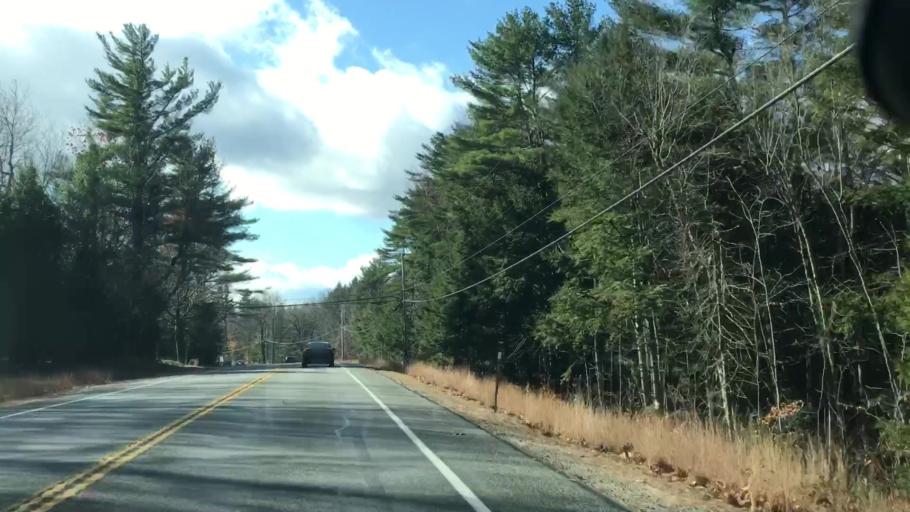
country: US
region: New Hampshire
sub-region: Carroll County
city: Ossipee
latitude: 43.6581
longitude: -71.1577
